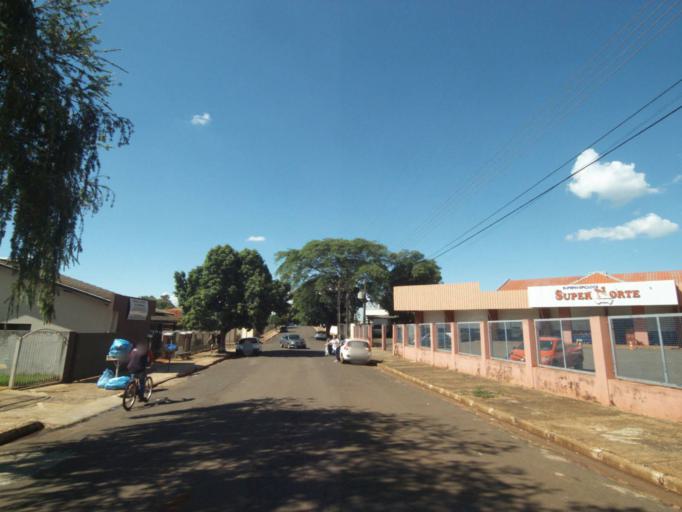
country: BR
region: Parana
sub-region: Sertanopolis
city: Sertanopolis
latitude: -23.0407
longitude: -50.8148
